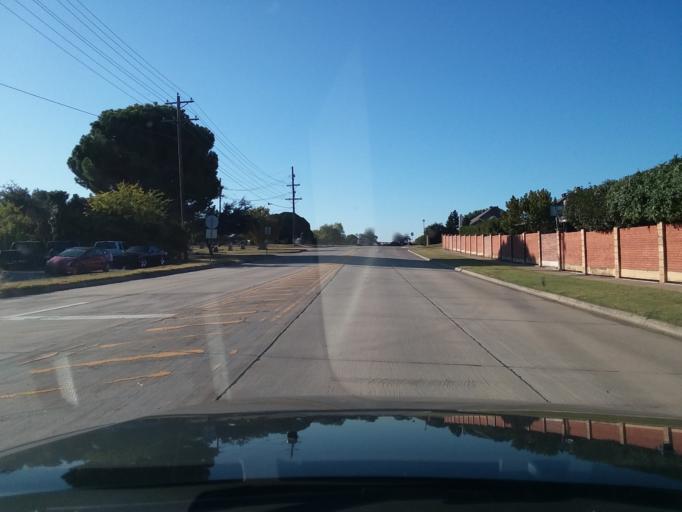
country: US
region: Texas
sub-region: Denton County
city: Highland Village
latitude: 33.0650
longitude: -97.0273
